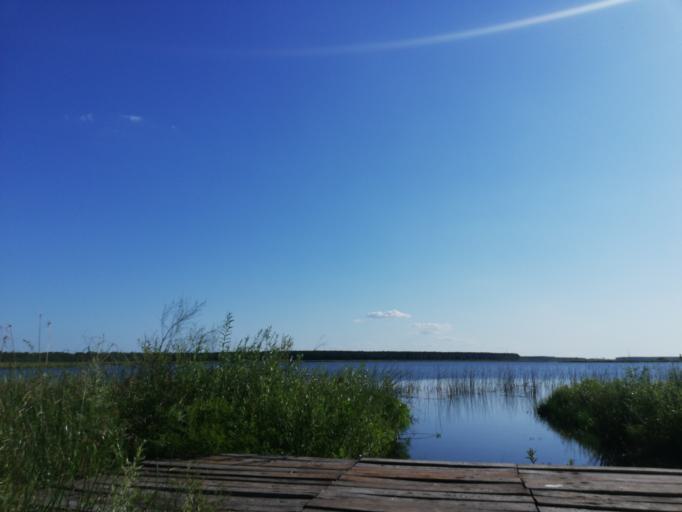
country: AR
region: Corrientes
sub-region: Departamento de San Miguel
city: San Miguel
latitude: -27.9903
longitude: -57.5421
